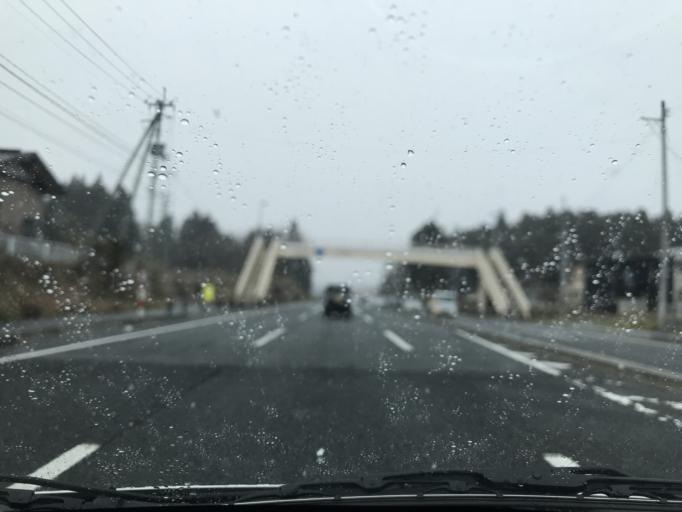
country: JP
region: Iwate
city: Kitakami
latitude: 39.2647
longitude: 141.0993
